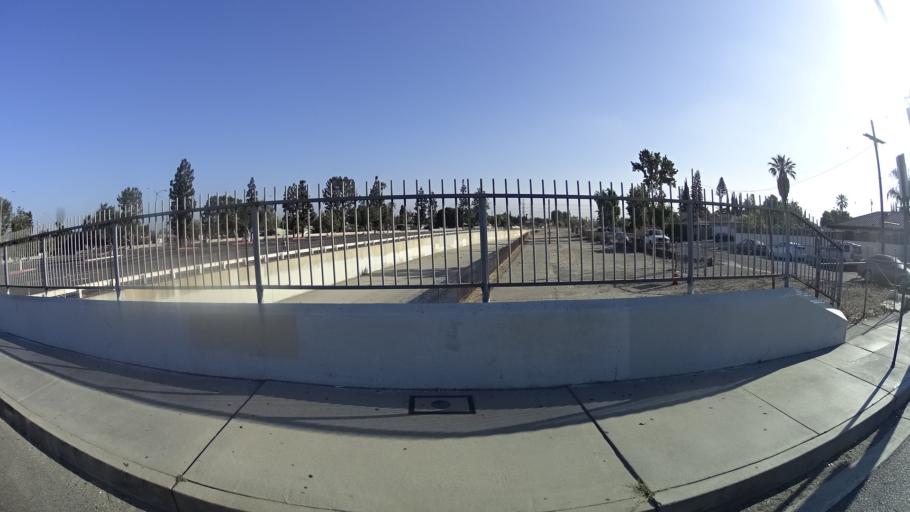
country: US
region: California
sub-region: Los Angeles County
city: Van Nuys
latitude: 34.2217
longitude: -118.4227
